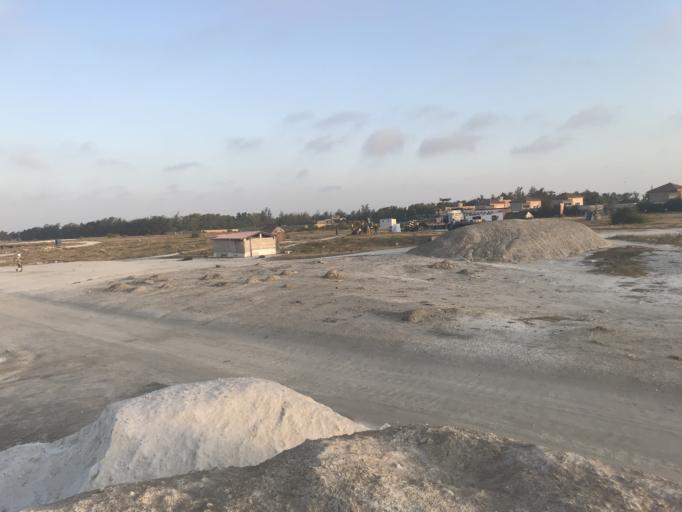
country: SN
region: Thies
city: Thies
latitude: 14.8334
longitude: -17.2382
